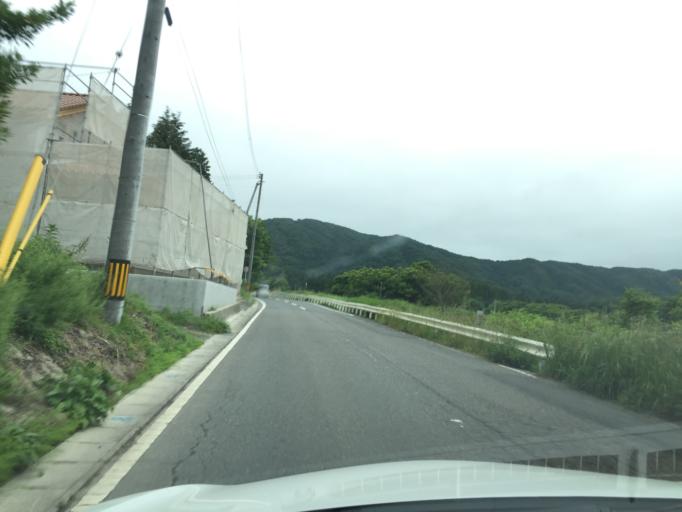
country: JP
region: Fukushima
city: Funehikimachi-funehiki
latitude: 37.3589
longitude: 140.6387
